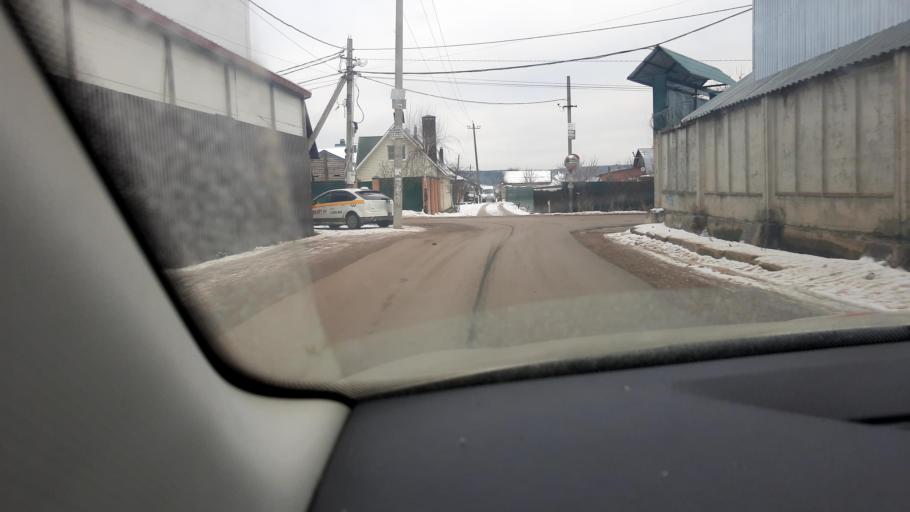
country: RU
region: Moskovskaya
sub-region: Leninskiy Rayon
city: Molokovo
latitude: 55.4899
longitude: 37.8562
